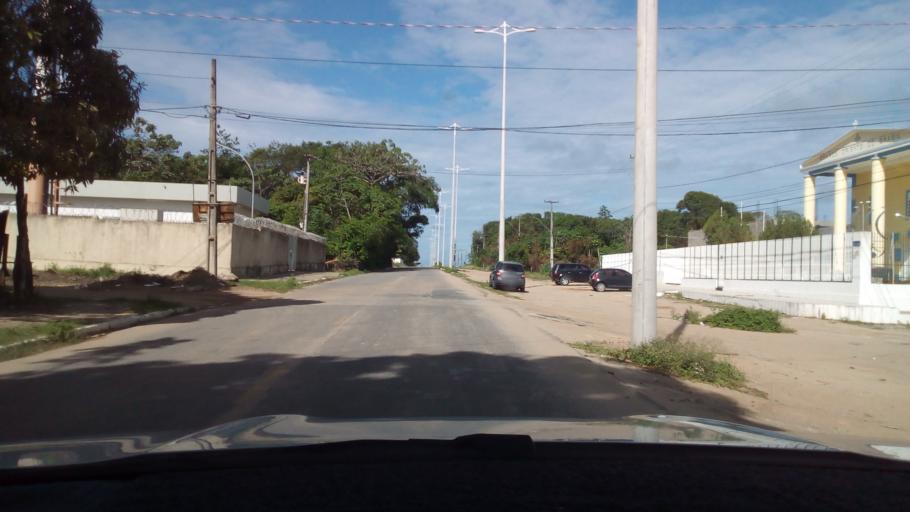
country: BR
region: Paraiba
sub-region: Joao Pessoa
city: Joao Pessoa
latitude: -7.1355
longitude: -34.8271
